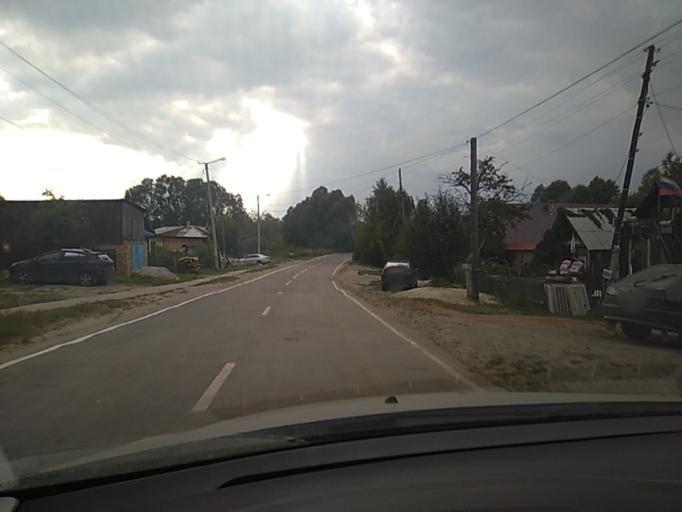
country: RU
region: Chelyabinsk
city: Kyshtym
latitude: 55.6969
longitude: 60.5457
